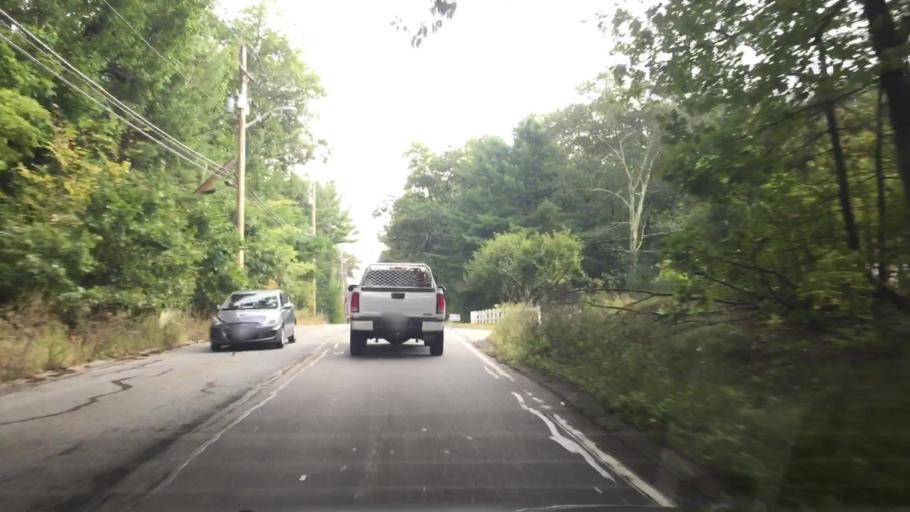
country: US
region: Massachusetts
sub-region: Middlesex County
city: Dracut
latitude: 42.6866
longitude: -71.2735
